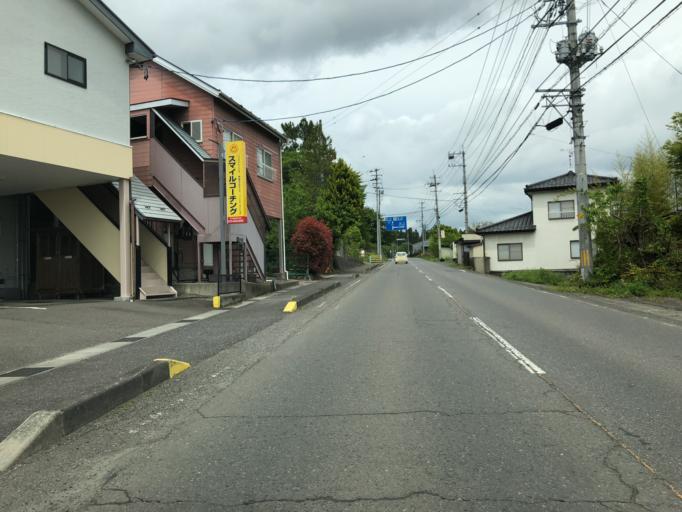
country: JP
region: Fukushima
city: Ishikawa
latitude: 37.0379
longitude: 140.3819
